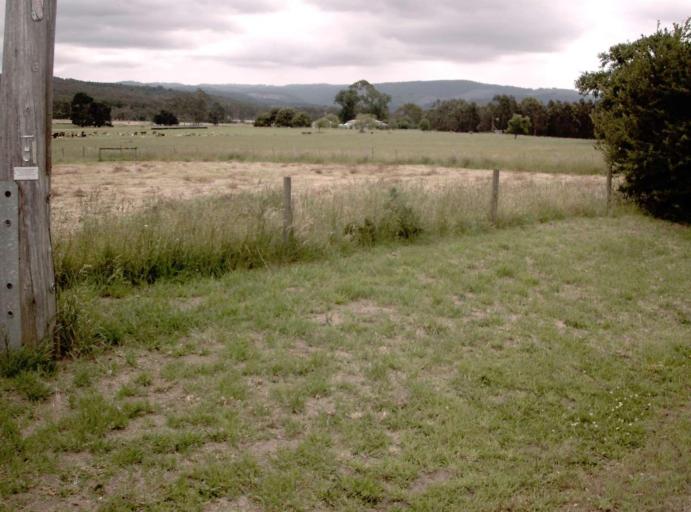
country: AU
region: Victoria
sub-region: Latrobe
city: Traralgon
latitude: -38.5142
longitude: 146.6621
